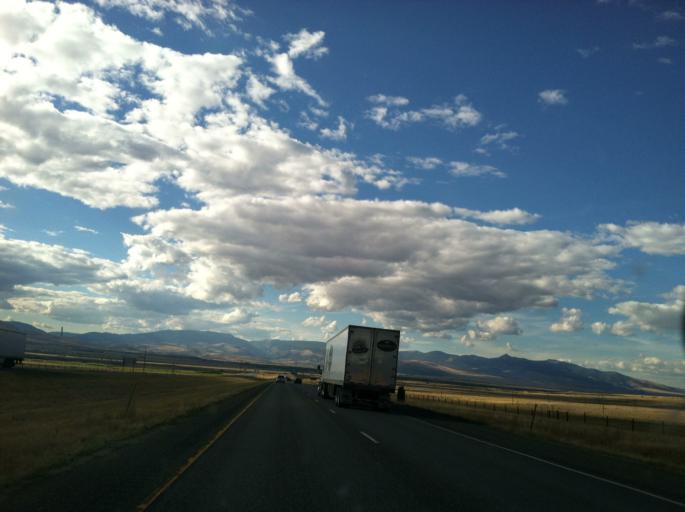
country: US
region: Montana
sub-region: Deer Lodge County
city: Warm Springs
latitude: 46.0592
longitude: -112.7648
